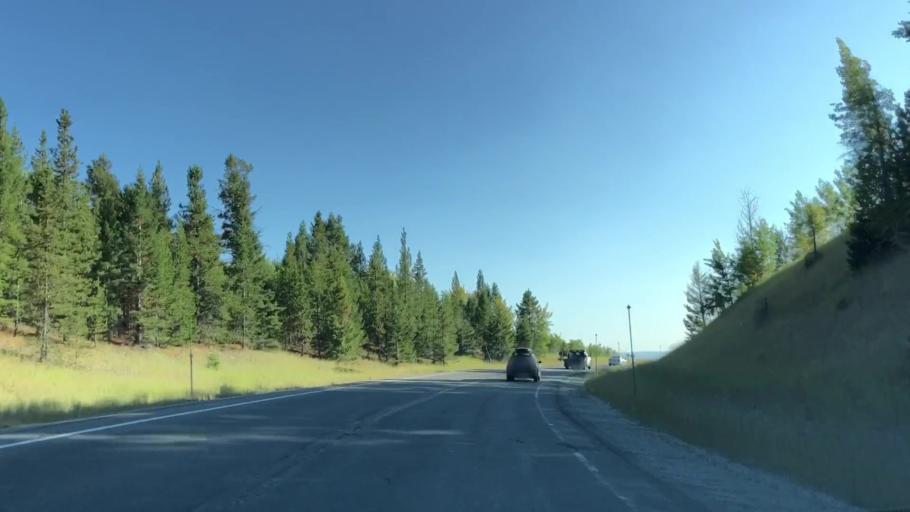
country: US
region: Montana
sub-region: Gallatin County
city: West Yellowstone
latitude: 44.7975
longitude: -111.1038
